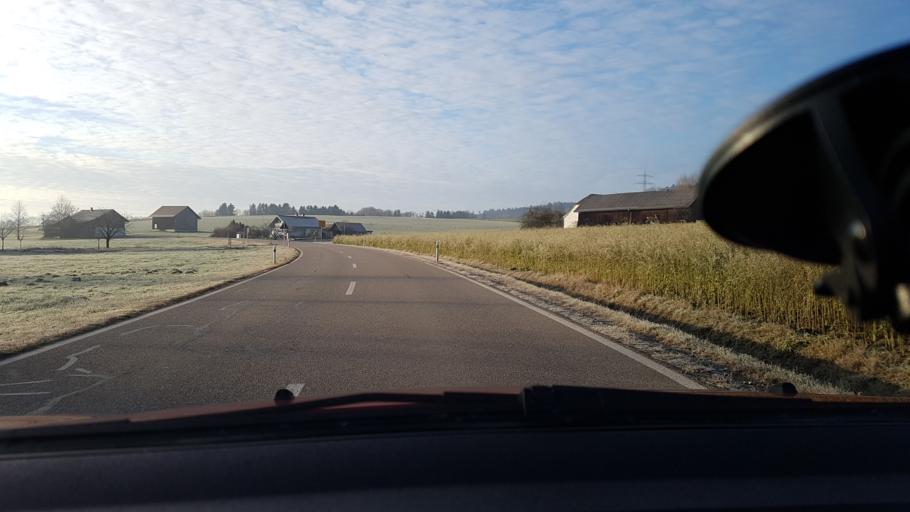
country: DE
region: Bavaria
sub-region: Lower Bavaria
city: Stubenberg
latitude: 48.3076
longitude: 13.0707
